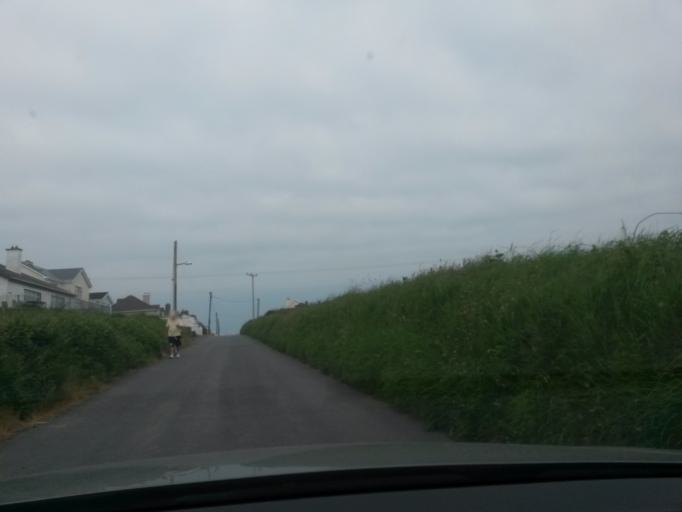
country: IE
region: Munster
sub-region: Ciarrai
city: Ballybunnion
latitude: 52.6776
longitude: -9.6623
